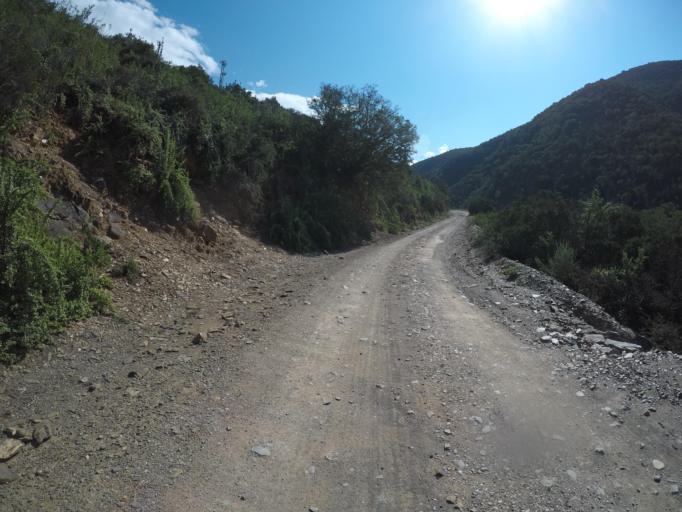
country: ZA
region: Eastern Cape
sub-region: Cacadu District Municipality
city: Kareedouw
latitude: -33.6550
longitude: 24.3575
